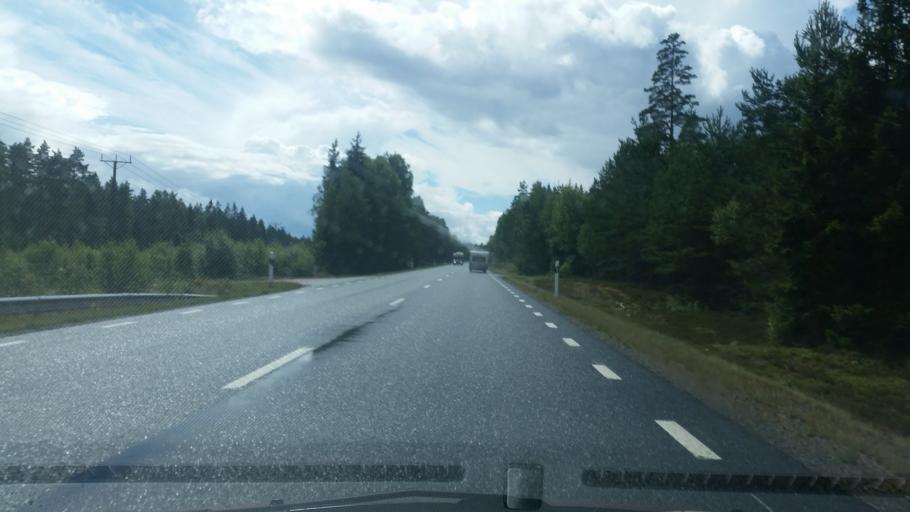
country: SE
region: Joenkoeping
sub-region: Gislaveds Kommun
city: Gislaved
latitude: 57.3948
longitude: 13.5917
